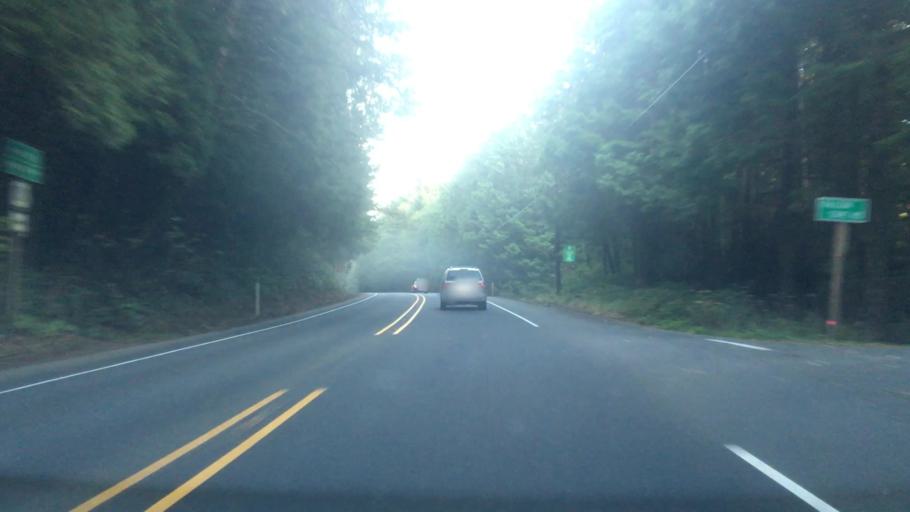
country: US
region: Oregon
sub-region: Clatsop County
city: Cannon Beach
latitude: 45.7820
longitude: -123.9566
